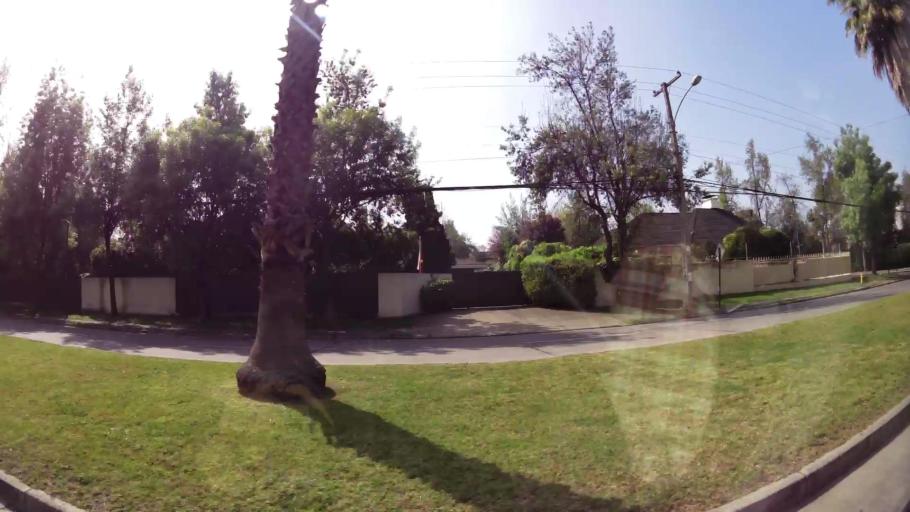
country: CL
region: Santiago Metropolitan
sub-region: Provincia de Santiago
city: Villa Presidente Frei, Nunoa, Santiago, Chile
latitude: -33.3783
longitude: -70.5834
